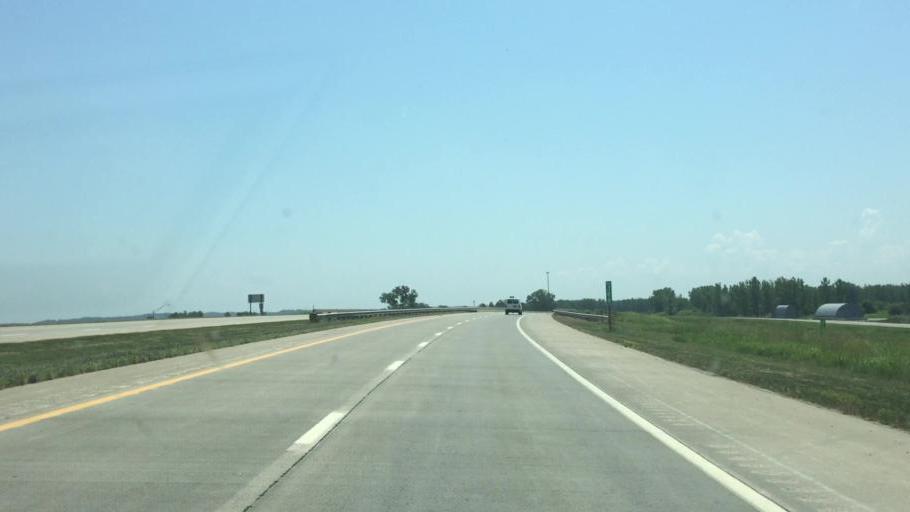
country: US
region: Kansas
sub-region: Doniphan County
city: Wathena
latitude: 39.7482
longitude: -94.9265
